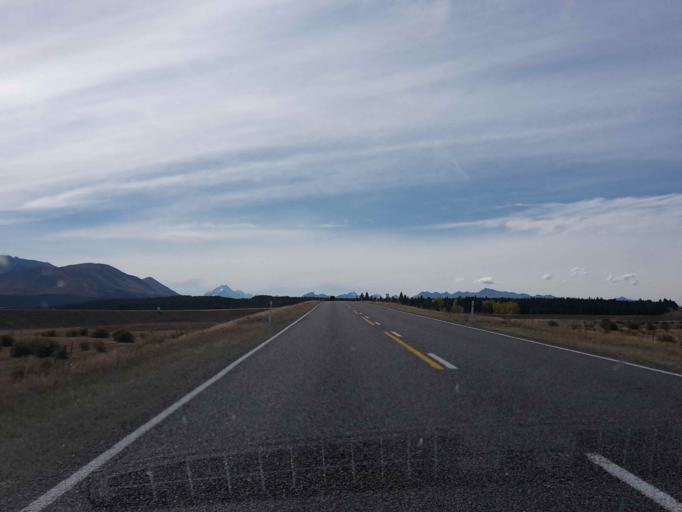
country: NZ
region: Canterbury
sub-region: Timaru District
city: Pleasant Point
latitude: -44.2059
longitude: 170.1188
